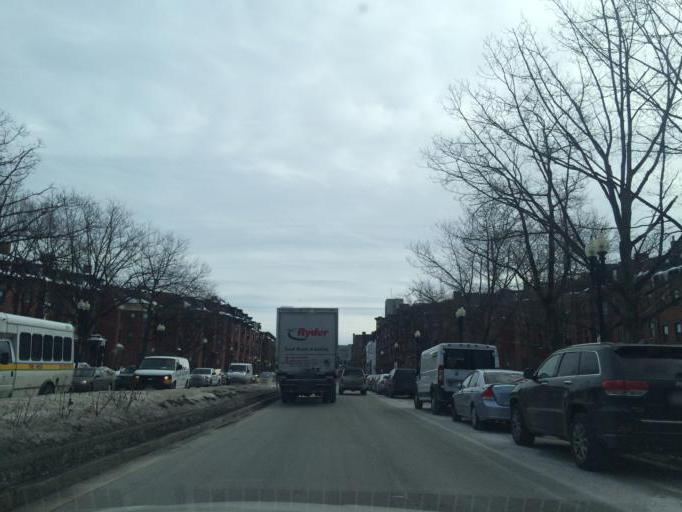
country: US
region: Massachusetts
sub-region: Suffolk County
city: Boston
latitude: 42.3386
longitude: -71.0795
